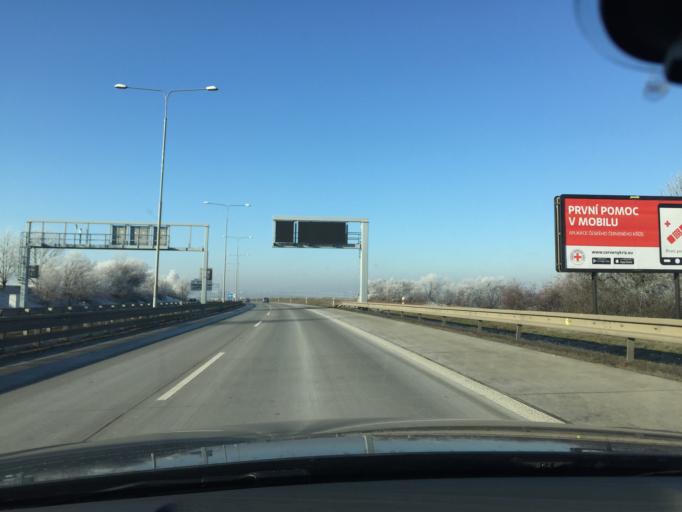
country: CZ
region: Central Bohemia
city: Trebotov
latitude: 50.0223
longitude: 14.3297
